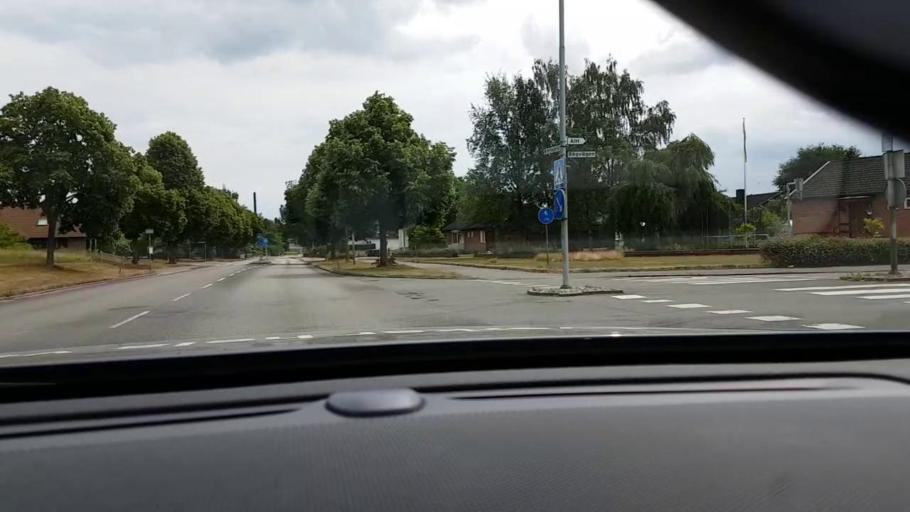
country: SE
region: Skane
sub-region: Hassleholms Kommun
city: Hassleholm
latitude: 56.1690
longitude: 13.7825
